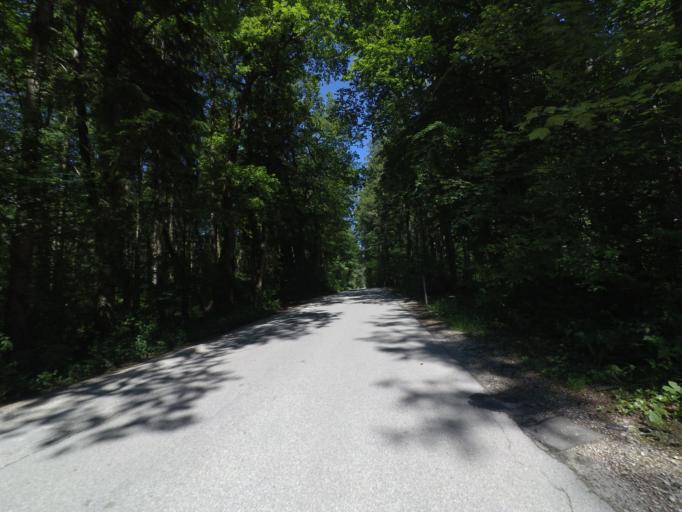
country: AT
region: Salzburg
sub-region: Politischer Bezirk Salzburg-Umgebung
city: Anif
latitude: 47.7578
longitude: 13.0424
